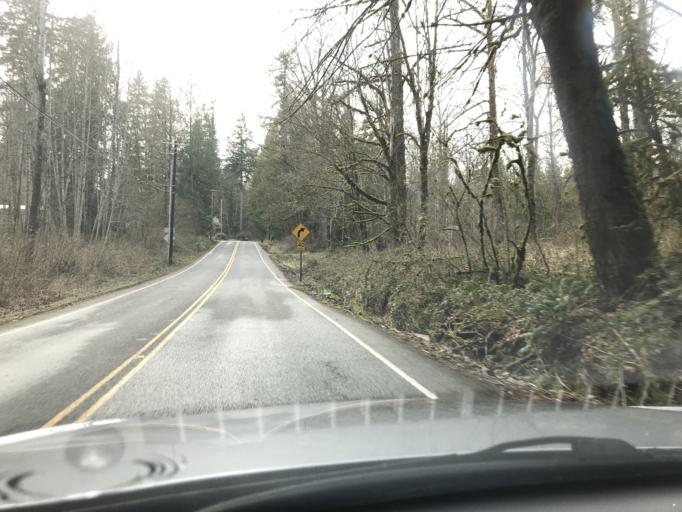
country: US
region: Washington
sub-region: King County
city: Ames Lake
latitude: 47.6490
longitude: -121.9703
